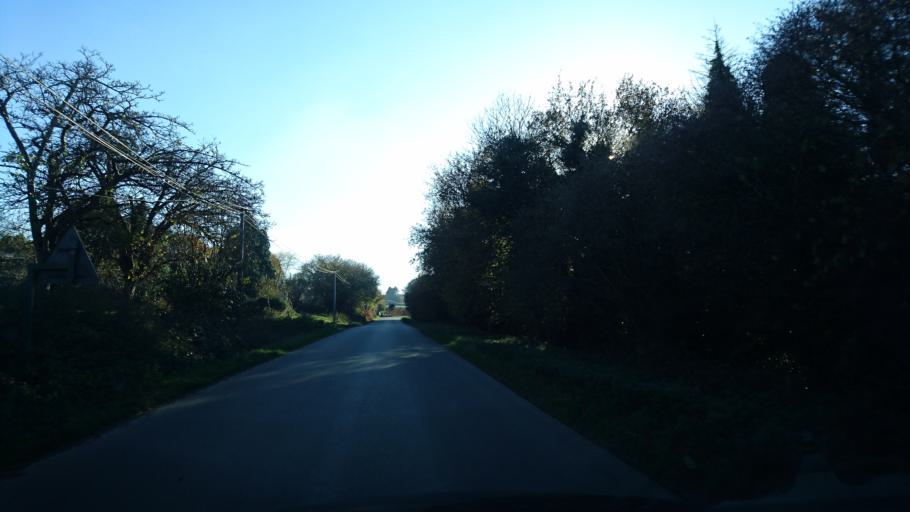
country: FR
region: Brittany
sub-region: Departement des Cotes-d'Armor
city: Pedernec
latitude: 48.5811
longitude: -3.2609
